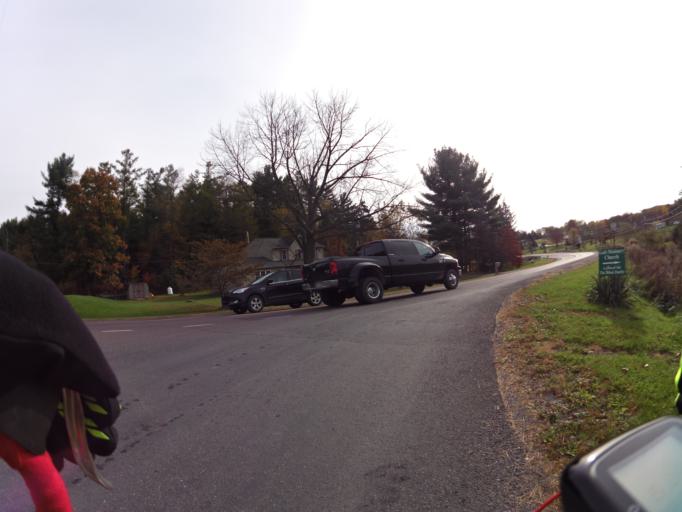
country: US
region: Pennsylvania
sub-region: Union County
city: New Columbia
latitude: 41.0454
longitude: -76.8825
